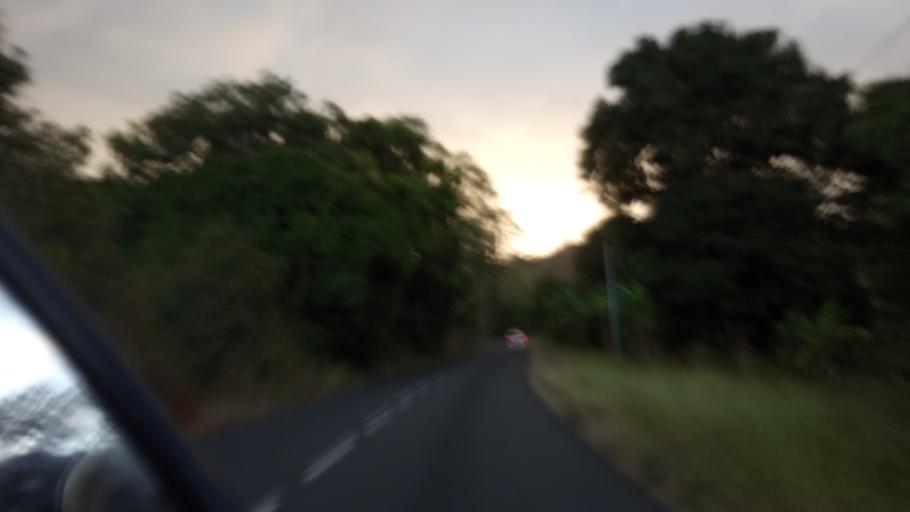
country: YT
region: Chirongui
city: Chirongui
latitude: -12.9306
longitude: 45.1212
